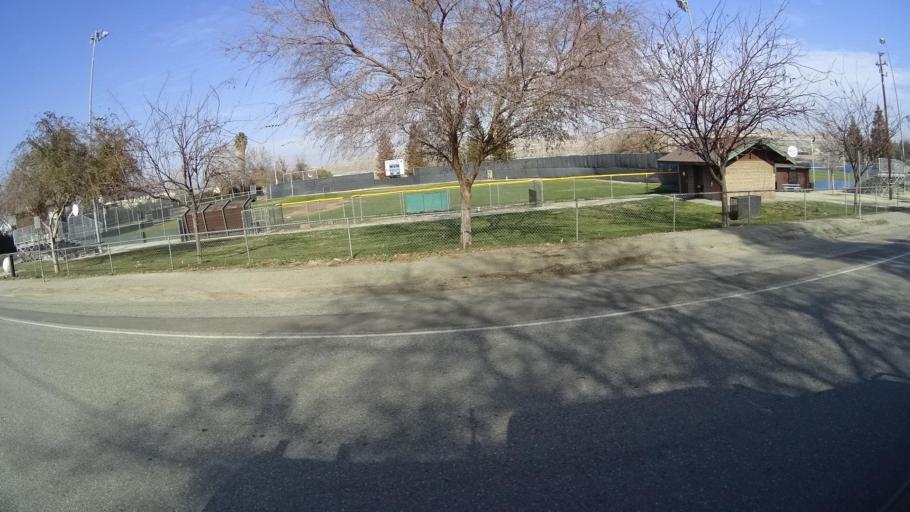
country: US
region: California
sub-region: Kern County
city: Ford City
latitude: 35.1546
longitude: -119.4417
